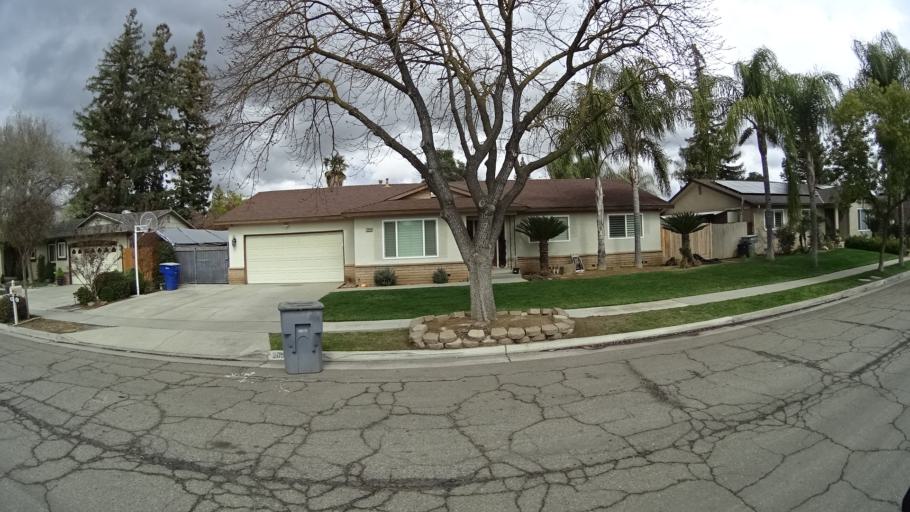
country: US
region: California
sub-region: Fresno County
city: Fresno
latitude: 36.8332
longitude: -119.8276
